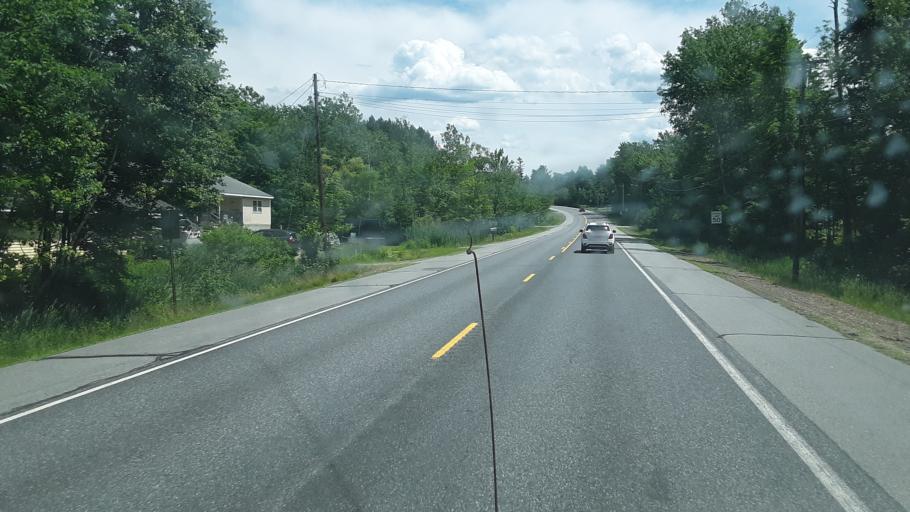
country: US
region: Maine
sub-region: Franklin County
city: Wilton
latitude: 44.5880
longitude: -70.2513
